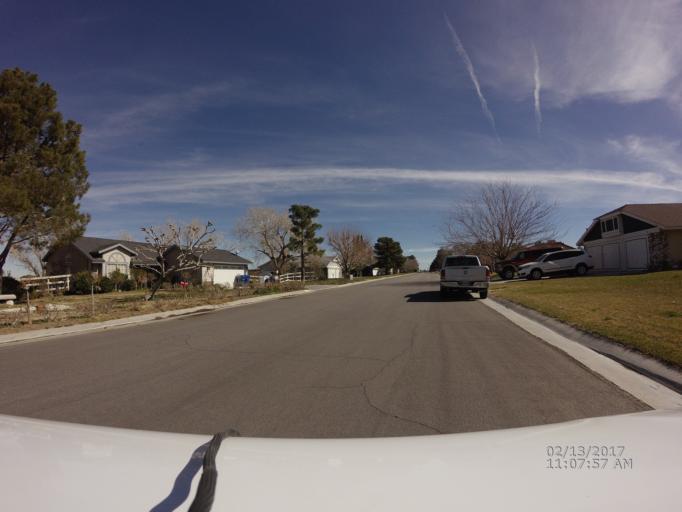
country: US
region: California
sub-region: Los Angeles County
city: Littlerock
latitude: 34.5255
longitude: -117.9968
